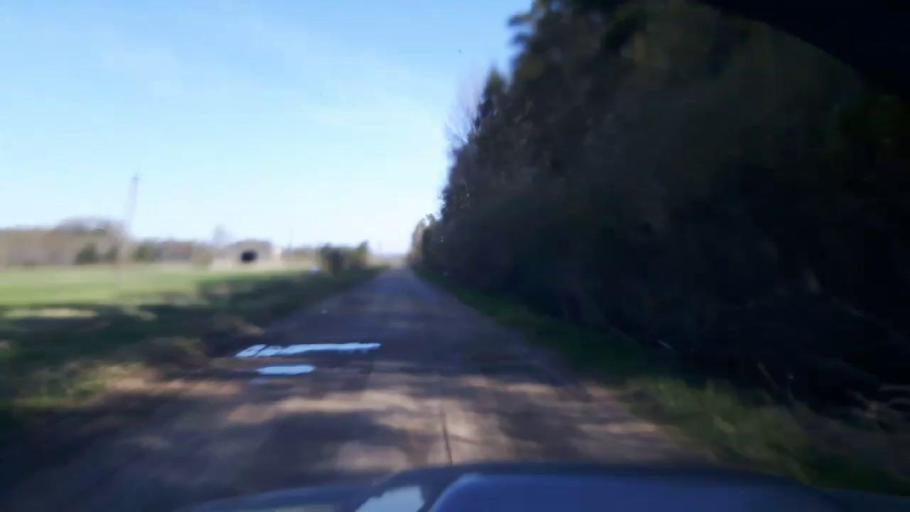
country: EE
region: Paernumaa
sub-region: Vaendra vald (alev)
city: Vandra
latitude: 58.5163
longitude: 24.9603
